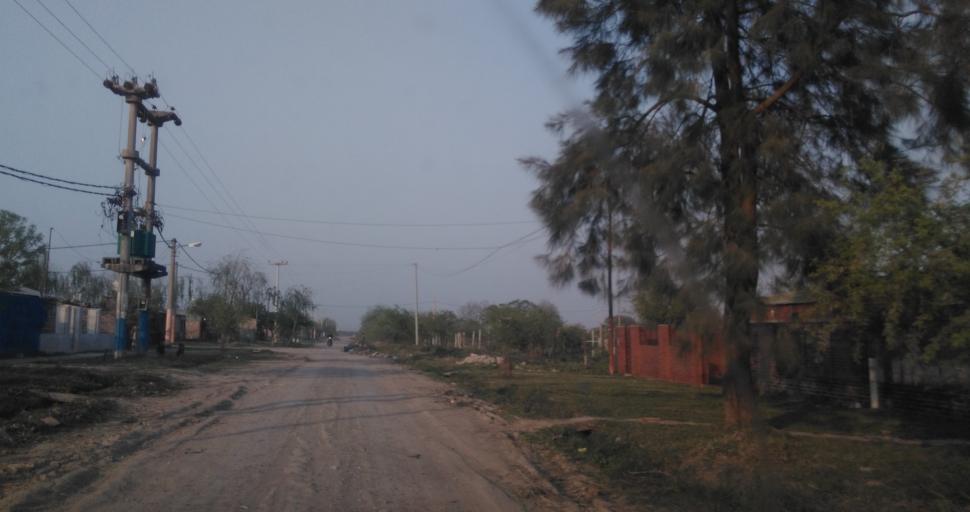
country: AR
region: Chaco
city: Resistencia
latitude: -27.4791
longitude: -59.0073
